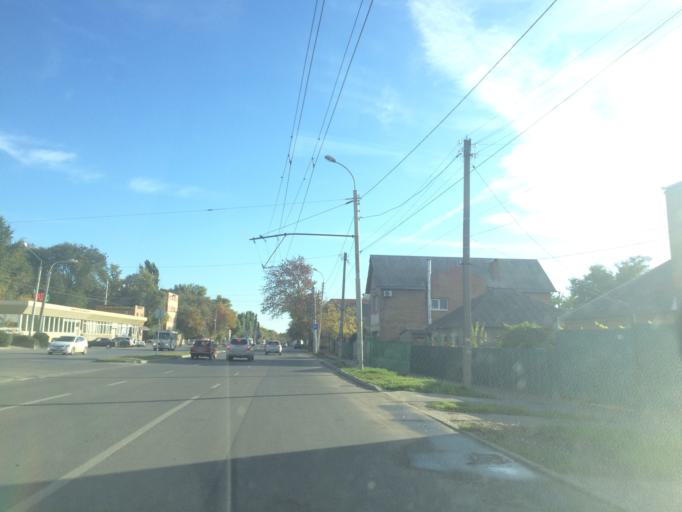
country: RU
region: Rostov
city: Rostov-na-Donu
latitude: 47.2020
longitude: 39.6699
